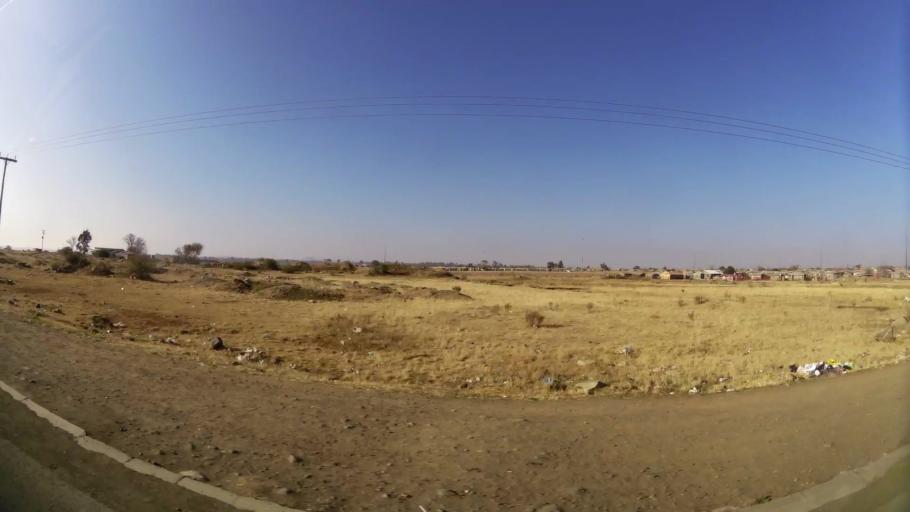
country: ZA
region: Orange Free State
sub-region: Mangaung Metropolitan Municipality
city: Bloemfontein
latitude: -29.1965
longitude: 26.2645
